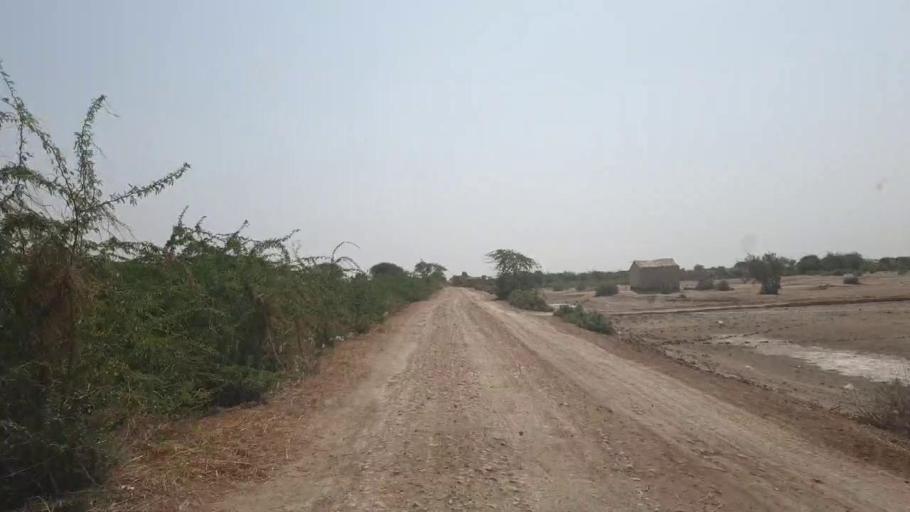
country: PK
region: Sindh
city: Jati
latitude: 24.4211
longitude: 68.5523
